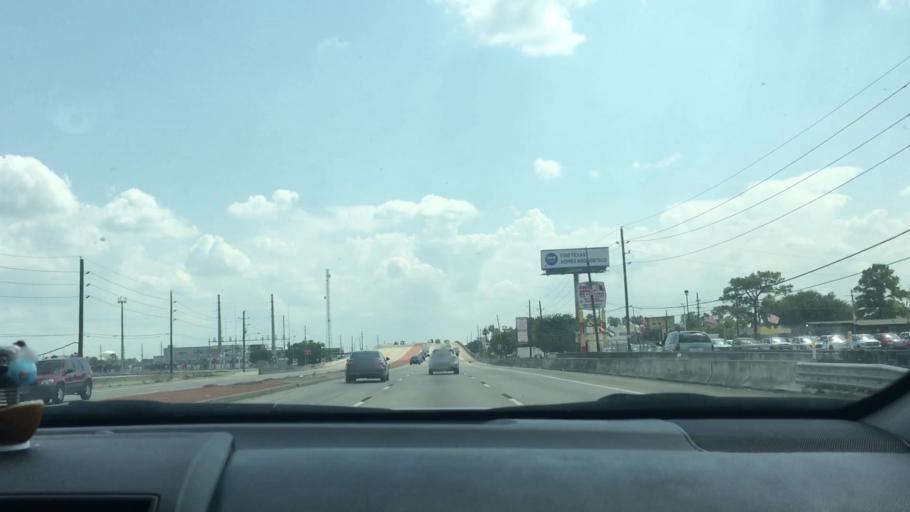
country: US
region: Texas
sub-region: Fort Bend County
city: Mission Bend
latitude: 29.7153
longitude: -95.6443
